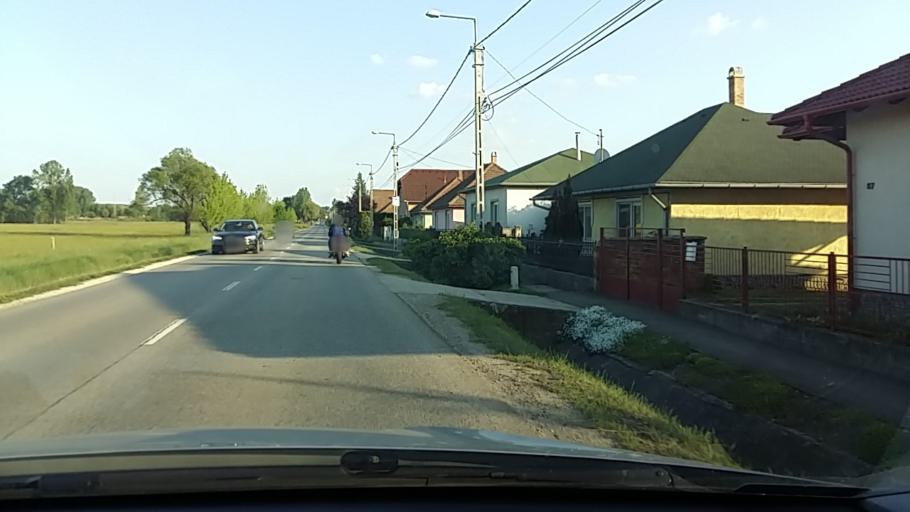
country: HU
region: Pest
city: Orbottyan
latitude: 47.7182
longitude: 19.2314
